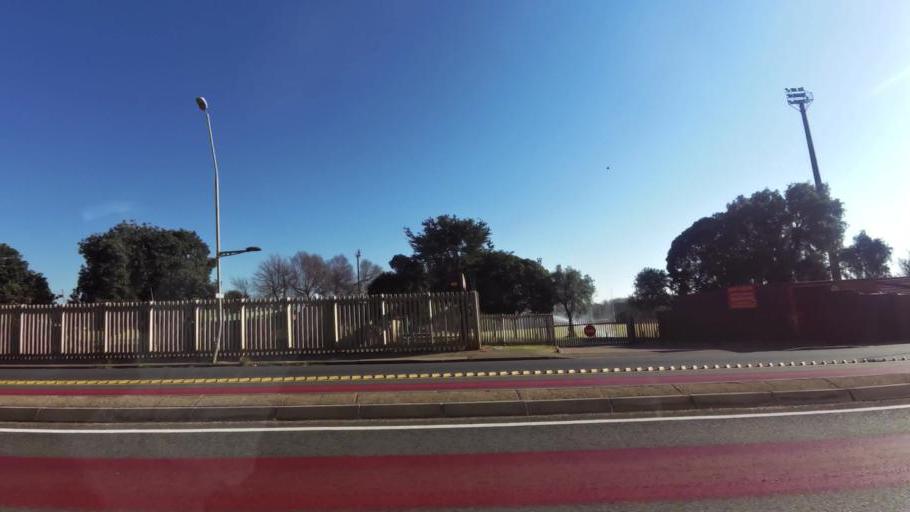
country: ZA
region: Gauteng
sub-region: City of Johannesburg Metropolitan Municipality
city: Johannesburg
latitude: -26.1849
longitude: 27.9865
